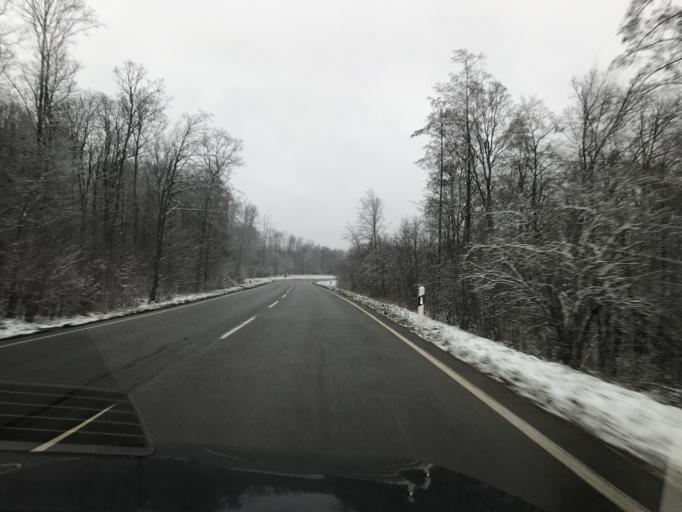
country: DE
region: Baden-Wuerttemberg
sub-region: Regierungsbezirk Stuttgart
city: Altbach
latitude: 48.7370
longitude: 9.3921
